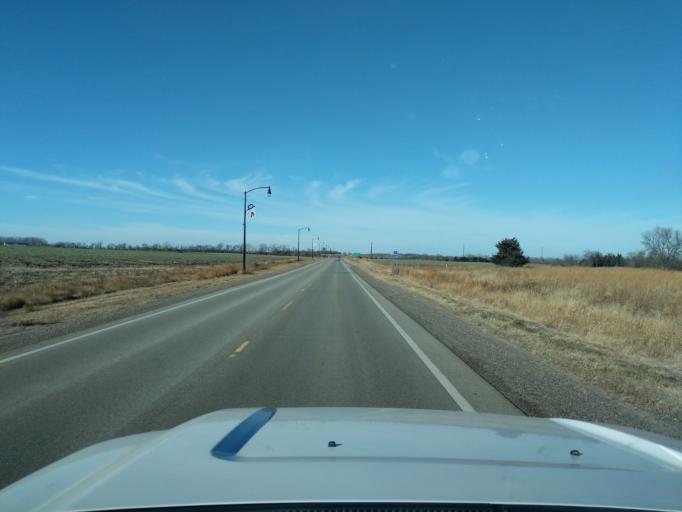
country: US
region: Minnesota
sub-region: Yellow Medicine County
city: Granite Falls
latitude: 44.7680
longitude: -95.5381
